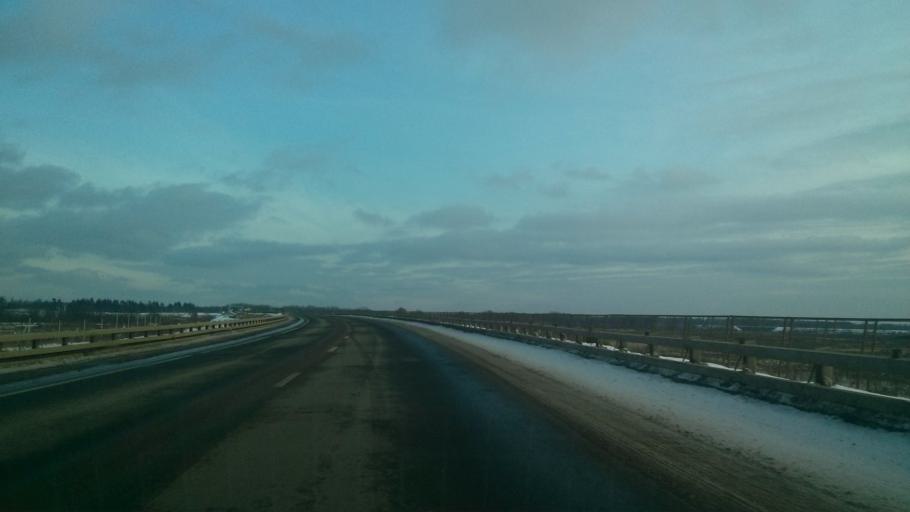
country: RU
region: Nizjnij Novgorod
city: Navashino
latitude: 55.5876
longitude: 42.1273
